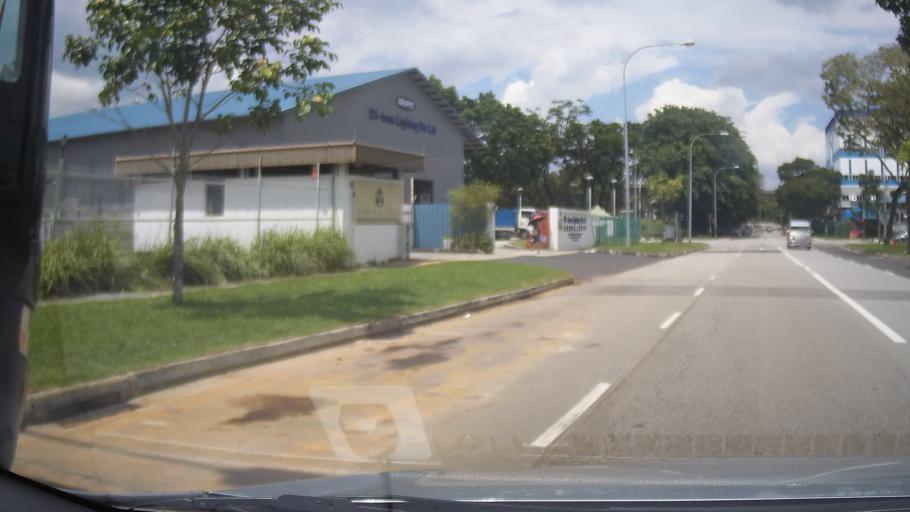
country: MY
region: Johor
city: Johor Bahru
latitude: 1.3268
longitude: 103.6880
